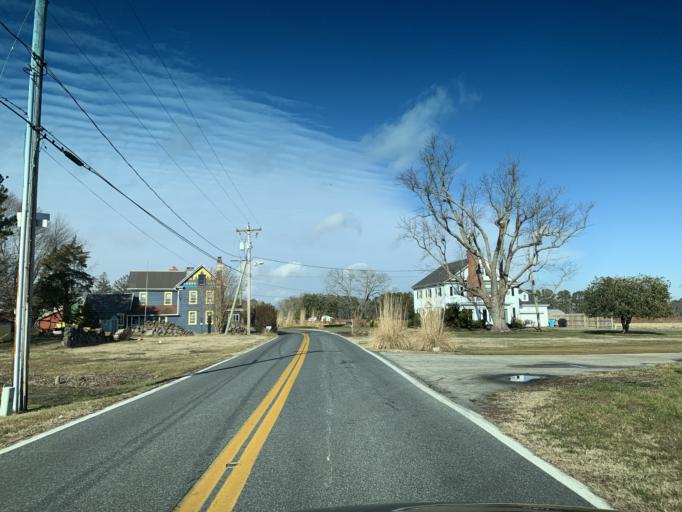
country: US
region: Delaware
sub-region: Sussex County
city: Selbyville
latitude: 38.4497
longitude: -75.1941
